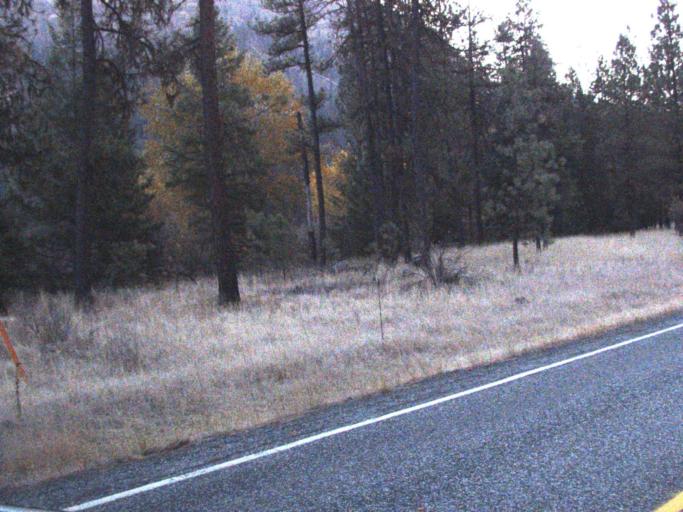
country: US
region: Washington
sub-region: Ferry County
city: Republic
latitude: 48.3256
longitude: -118.7444
